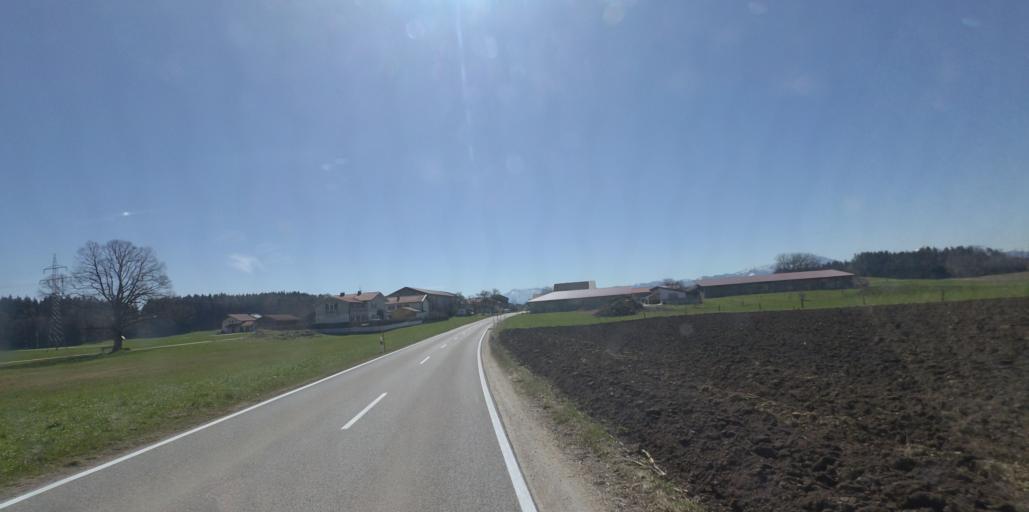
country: DE
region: Bavaria
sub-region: Upper Bavaria
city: Nussdorf
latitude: 47.8992
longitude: 12.6039
